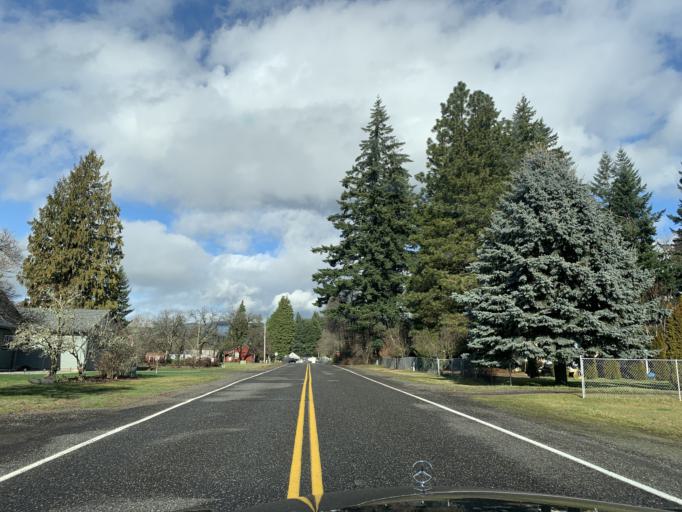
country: US
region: Washington
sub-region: Skamania County
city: Carson
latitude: 45.7235
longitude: -121.8163
